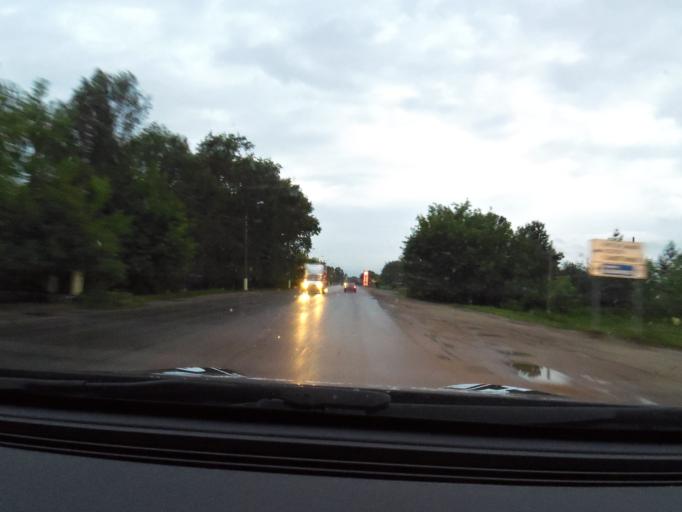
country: RU
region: Vladimir
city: Aleksandrov
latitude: 56.3964
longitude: 38.7601
